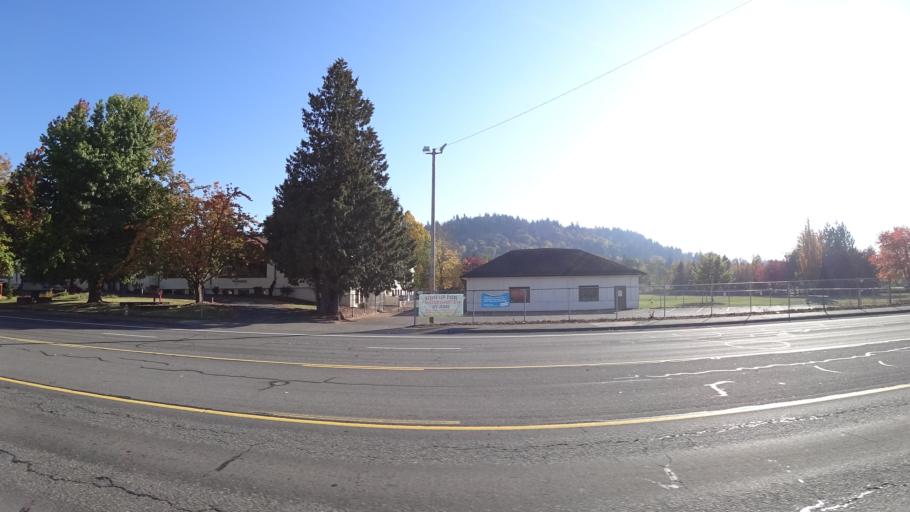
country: US
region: Oregon
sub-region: Multnomah County
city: Gresham
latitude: 45.4972
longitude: -122.4359
